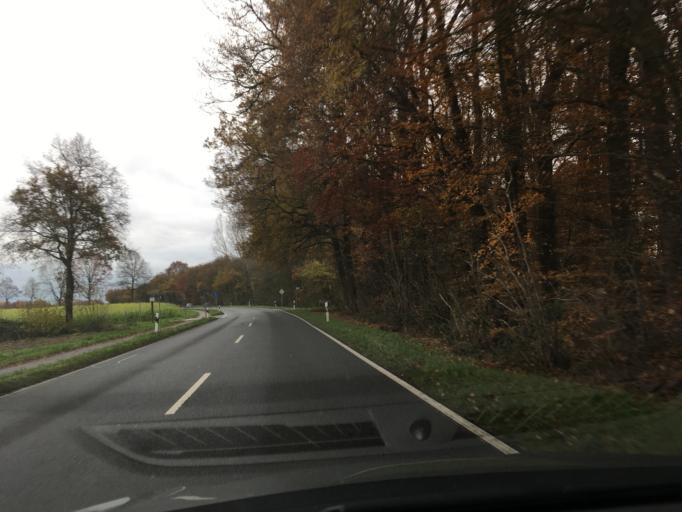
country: DE
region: North Rhine-Westphalia
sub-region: Regierungsbezirk Munster
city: Ahaus
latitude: 52.0791
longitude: 6.9740
